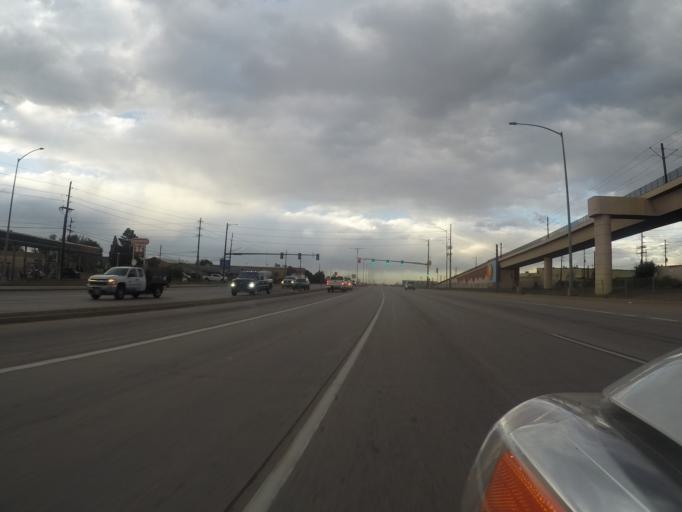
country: US
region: Colorado
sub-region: Arapahoe County
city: Littleton
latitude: 39.6314
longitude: -105.0088
